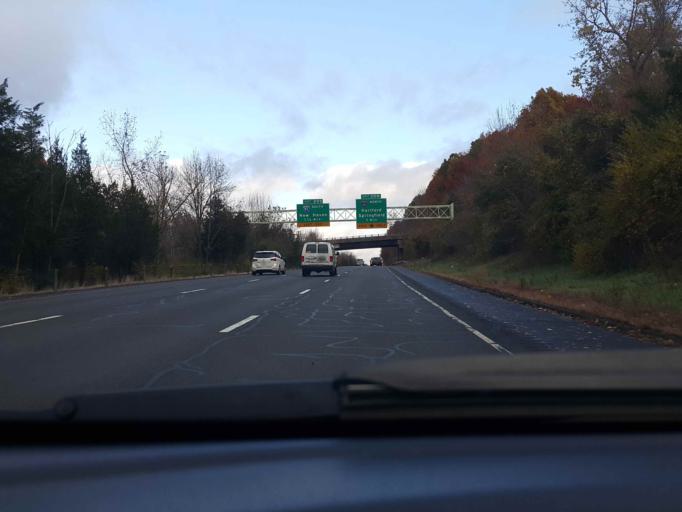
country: US
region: Connecticut
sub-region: Middlesex County
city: Cromwell
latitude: 41.6103
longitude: -72.6772
